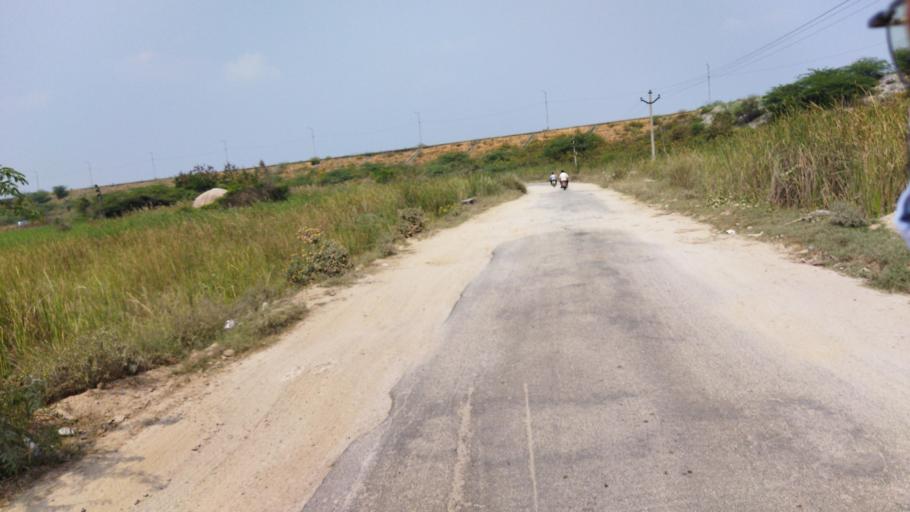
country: IN
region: Telangana
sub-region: Nalgonda
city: Nalgonda
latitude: 17.0760
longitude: 79.3143
